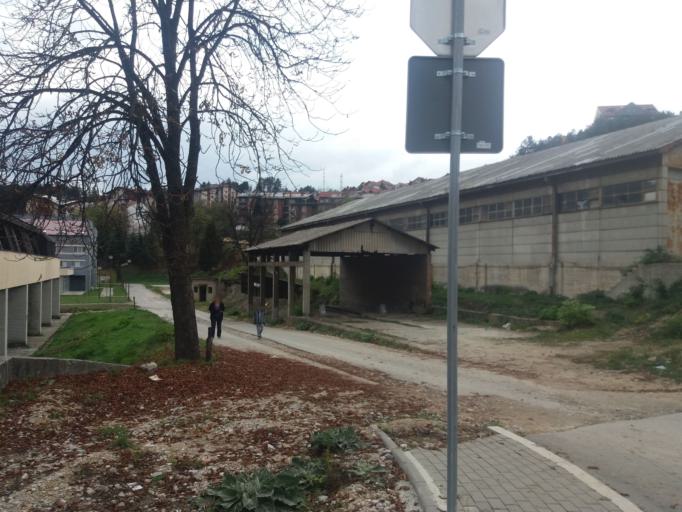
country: RS
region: Central Serbia
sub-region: Zlatiborski Okrug
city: Uzice
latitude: 43.8538
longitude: 19.8557
